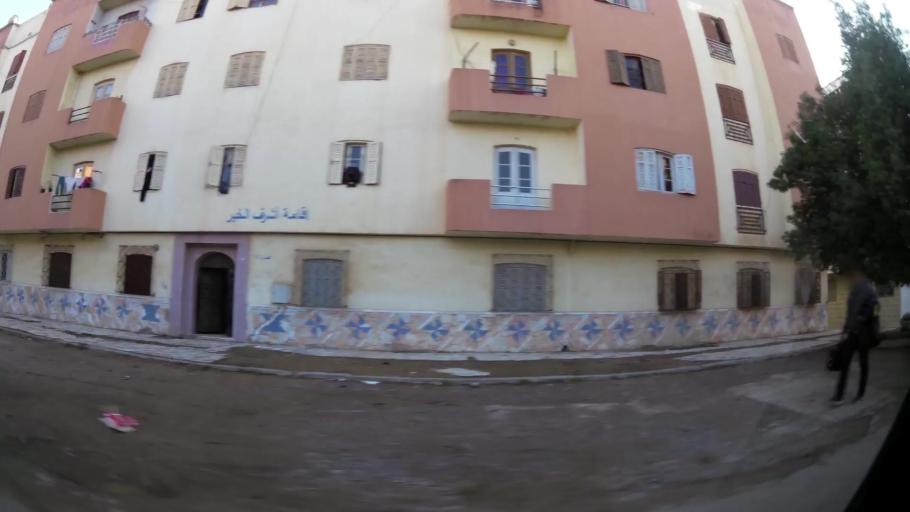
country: MA
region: Chaouia-Ouardigha
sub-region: Settat Province
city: Settat
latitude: 32.9877
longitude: -7.6091
